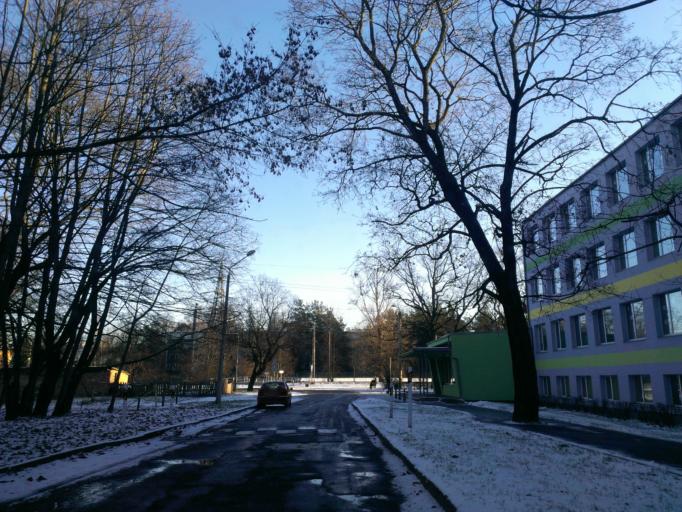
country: LV
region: Riga
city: Jaunciems
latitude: 57.0064
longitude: 24.1236
